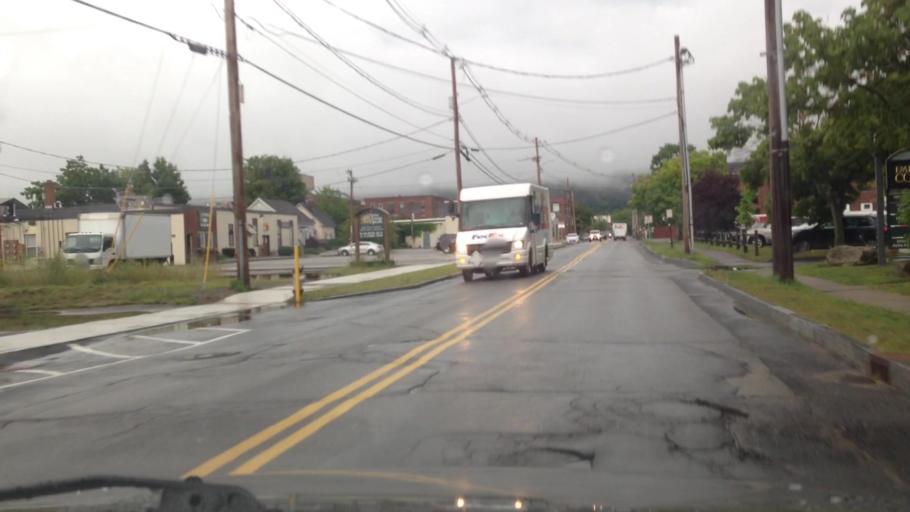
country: US
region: New Hampshire
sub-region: Cheshire County
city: Keene
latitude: 42.9306
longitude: -72.2816
